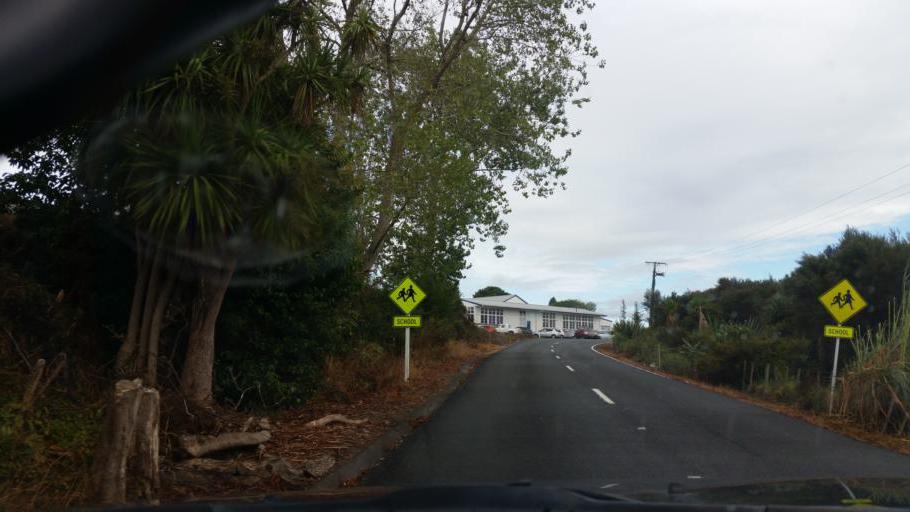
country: NZ
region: Auckland
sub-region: Auckland
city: Wellsford
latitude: -36.1178
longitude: 174.3662
